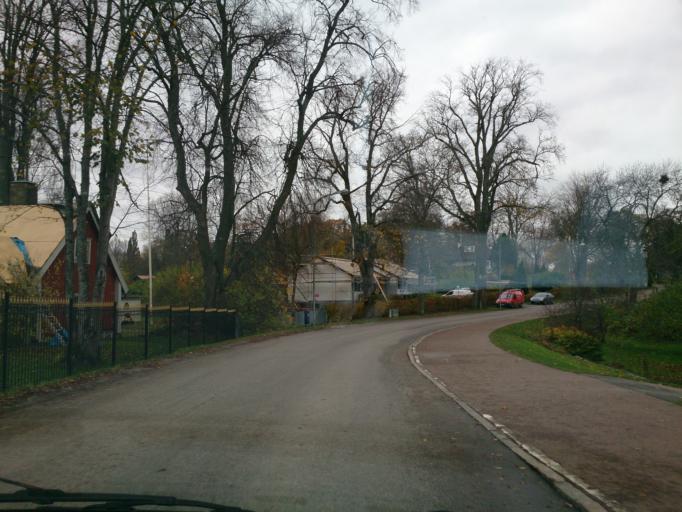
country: SE
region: OEstergoetland
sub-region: Atvidabergs Kommun
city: Atvidaberg
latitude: 58.1944
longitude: 15.9929
